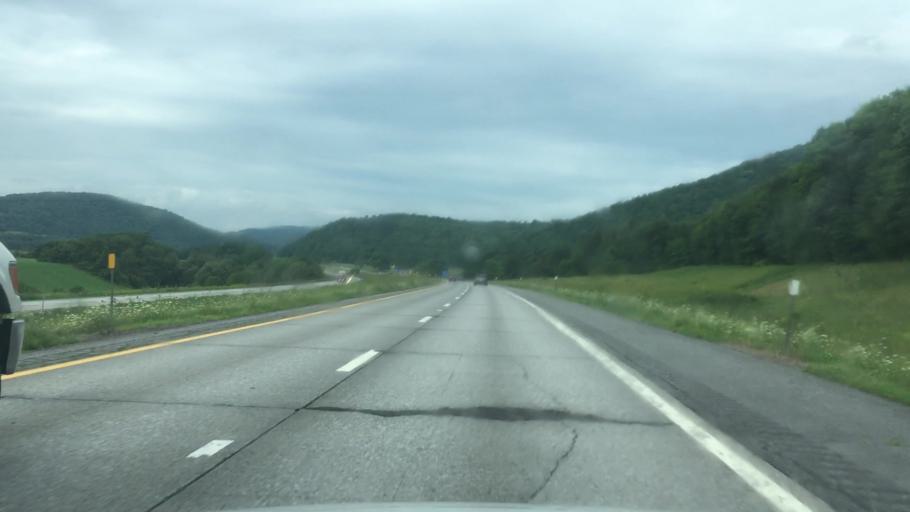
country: US
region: New York
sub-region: Otsego County
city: Worcester
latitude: 42.5639
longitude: -74.7741
